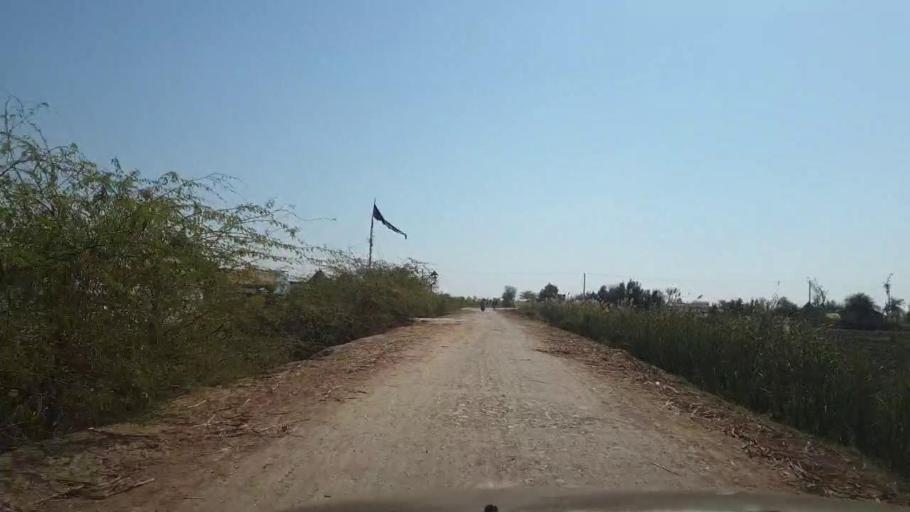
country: PK
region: Sindh
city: Mirpur Khas
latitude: 25.5671
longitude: 69.0754
